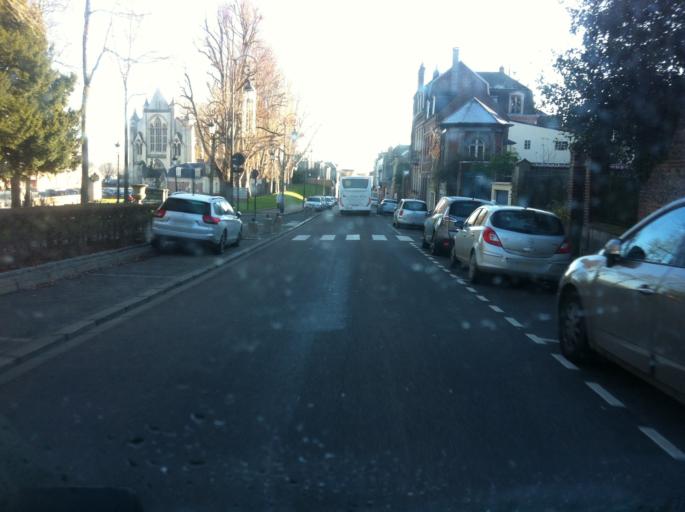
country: FR
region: Haute-Normandie
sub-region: Departement de la Seine-Maritime
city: Eu
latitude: 50.0485
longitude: 1.4162
